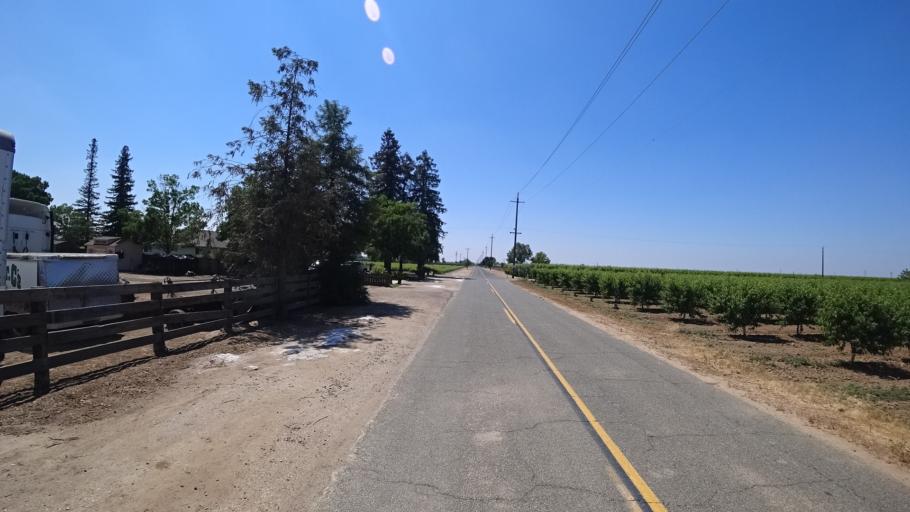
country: US
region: California
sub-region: Fresno County
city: Kingsburg
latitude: 36.4747
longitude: -119.5821
